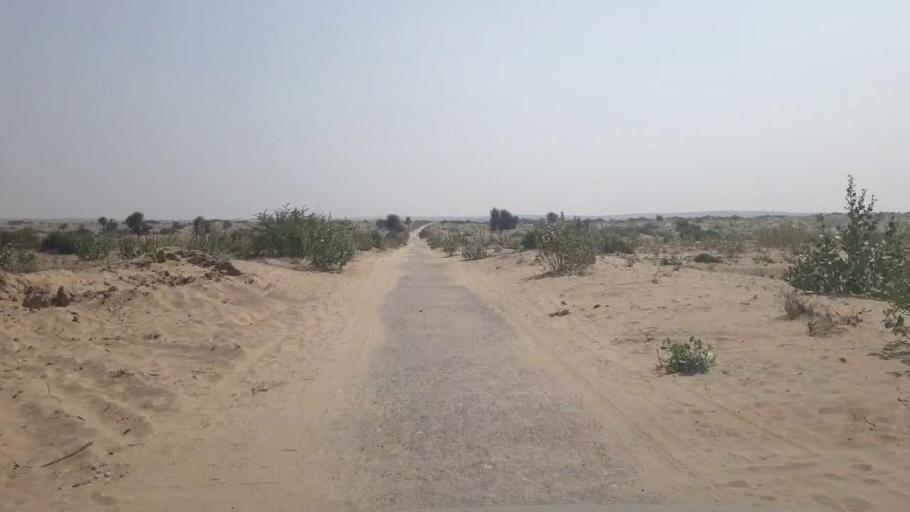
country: PK
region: Sindh
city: Chor
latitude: 25.4637
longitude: 69.7790
